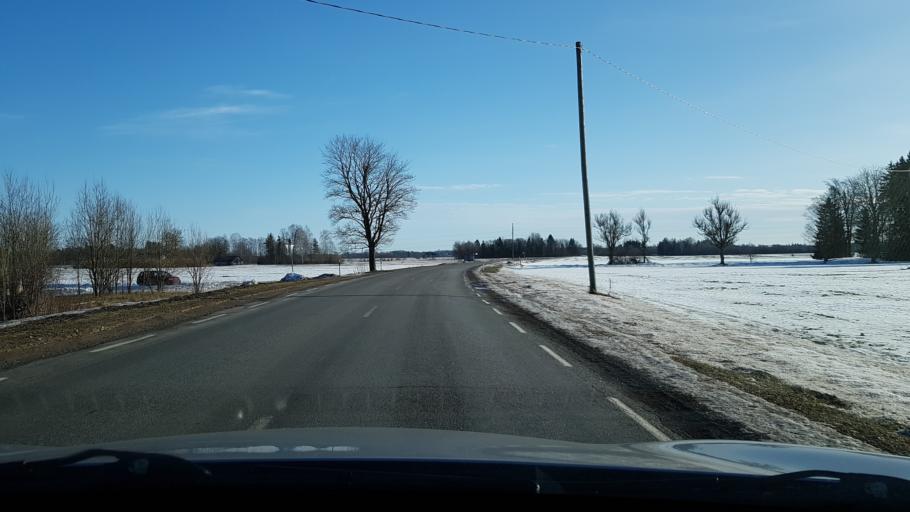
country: EE
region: Viljandimaa
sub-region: Vohma linn
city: Vohma
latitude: 58.6326
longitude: 25.6071
